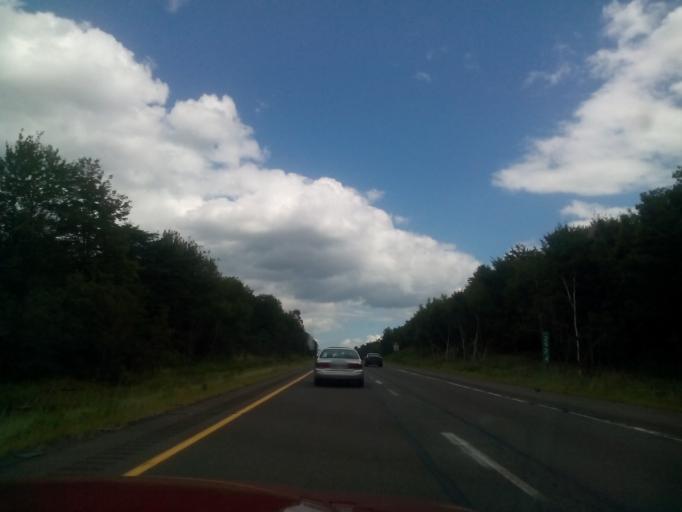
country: US
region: Pennsylvania
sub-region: Monroe County
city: Emerald Lakes
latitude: 41.0709
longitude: -75.4126
